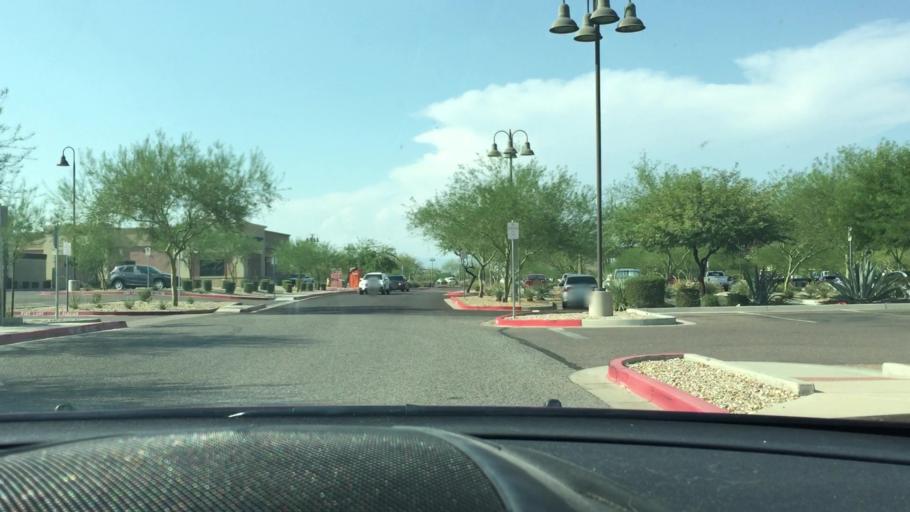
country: US
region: Arizona
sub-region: Maricopa County
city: Sun City West
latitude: 33.7114
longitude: -112.2697
